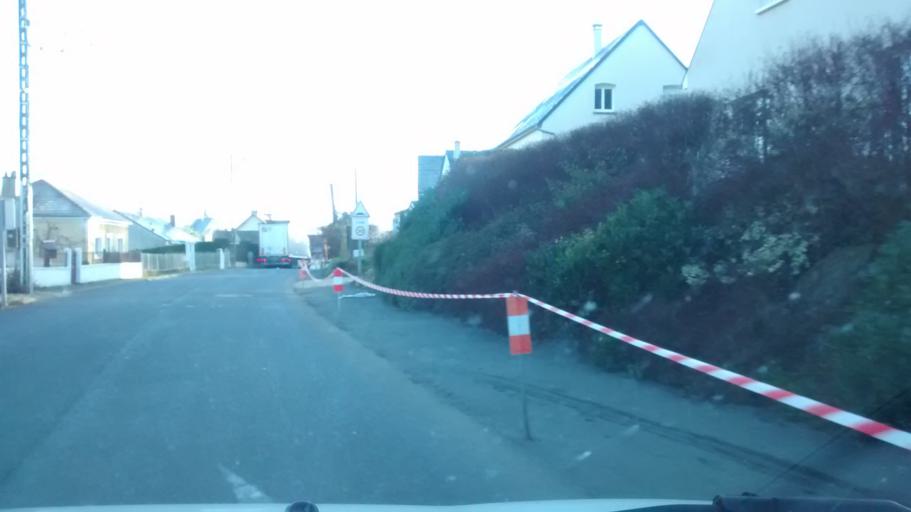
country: FR
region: Centre
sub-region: Departement d'Indre-et-Loire
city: Reugny
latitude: 47.4827
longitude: 0.8788
